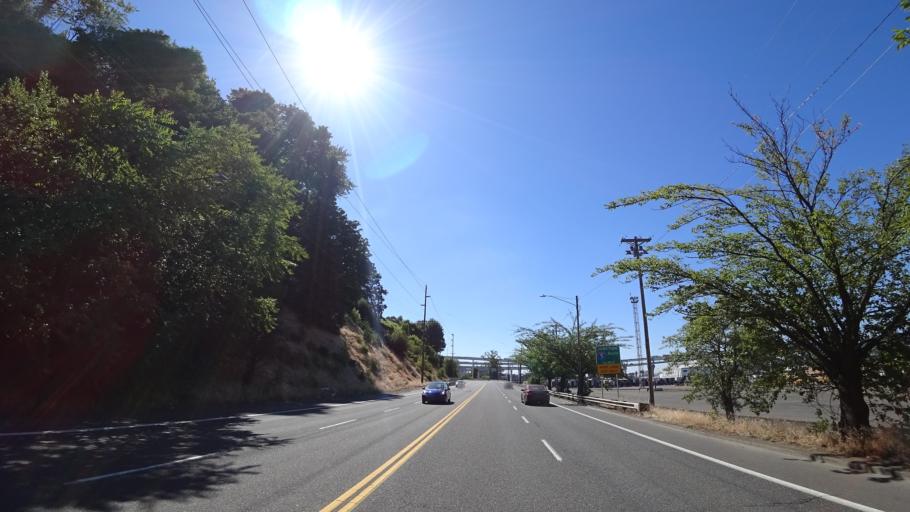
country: US
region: Oregon
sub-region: Multnomah County
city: Portland
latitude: 45.5475
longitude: -122.6842
